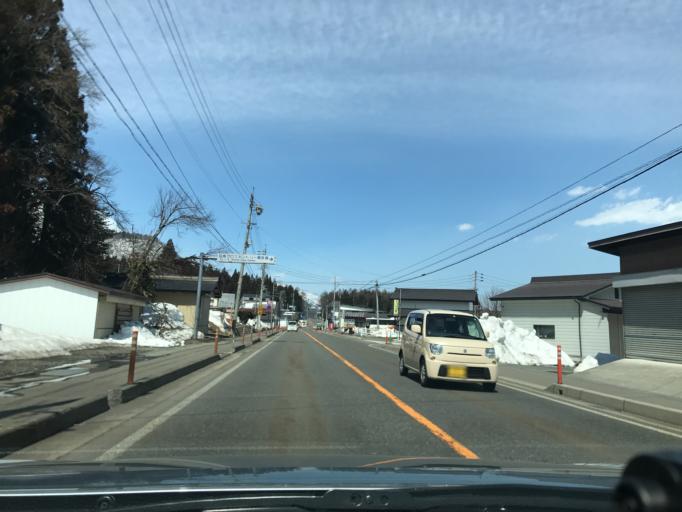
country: JP
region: Nagano
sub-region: Kitaazumi Gun
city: Hakuba
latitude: 36.6336
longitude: 137.8447
